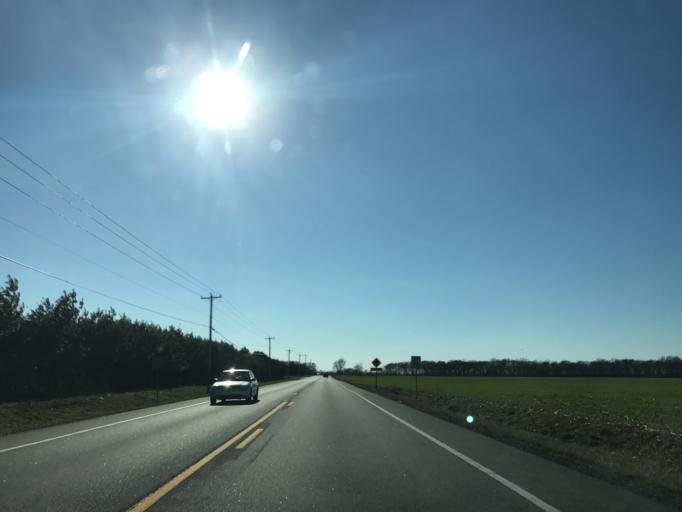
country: US
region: Maryland
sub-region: Caroline County
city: Ridgely
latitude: 39.0328
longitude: -75.8869
